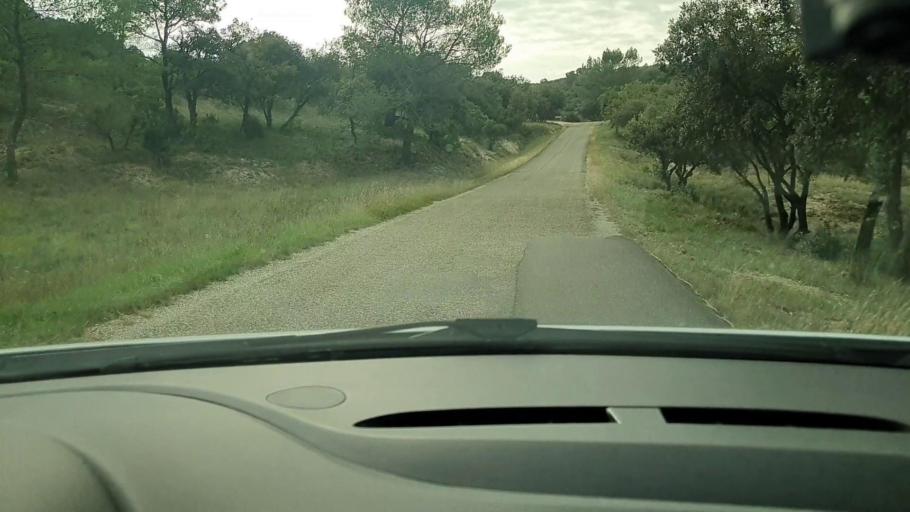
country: FR
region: Languedoc-Roussillon
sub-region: Departement du Gard
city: Montaren-et-Saint-Mediers
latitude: 44.0938
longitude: 4.3264
